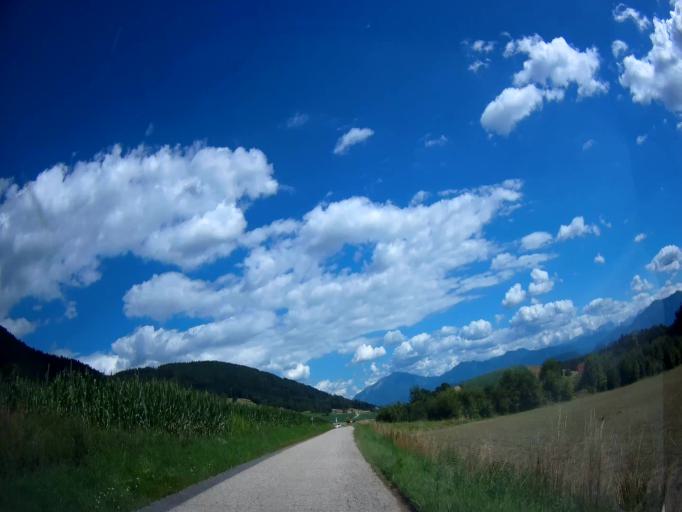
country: AT
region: Carinthia
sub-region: Politischer Bezirk Klagenfurt Land
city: Poggersdorf
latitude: 46.6754
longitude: 14.5196
